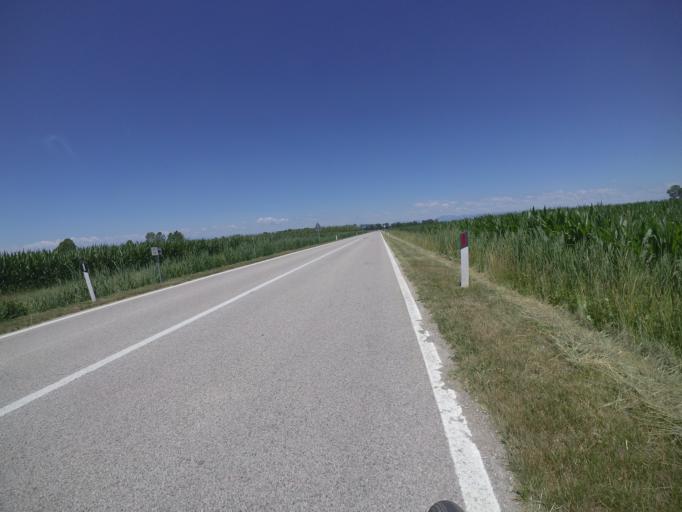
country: IT
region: Friuli Venezia Giulia
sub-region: Provincia di Udine
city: Talmassons
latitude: 45.9043
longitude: 13.0814
